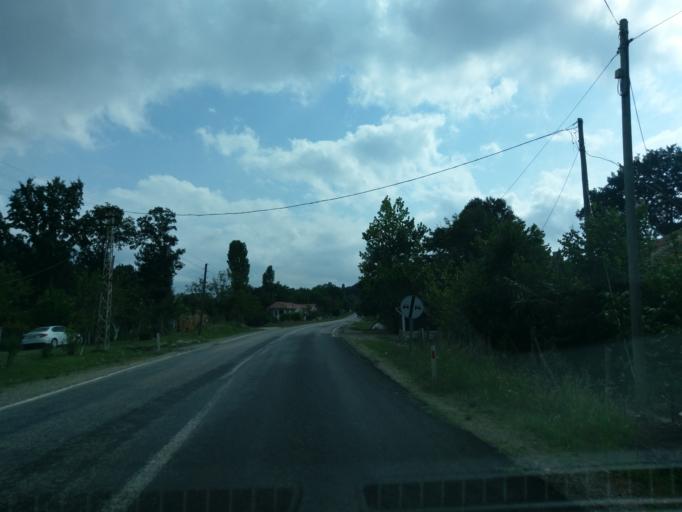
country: TR
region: Sinop
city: Erfelek
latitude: 41.9463
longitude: 34.7852
